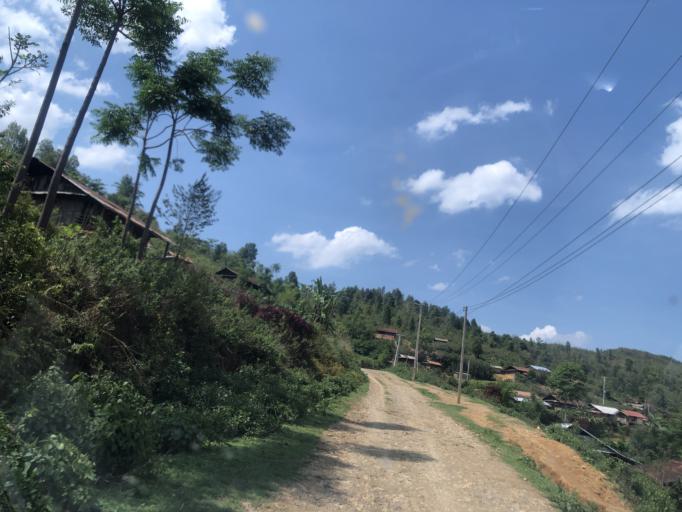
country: LA
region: Phongsali
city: Phongsali
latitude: 21.4050
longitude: 102.2326
